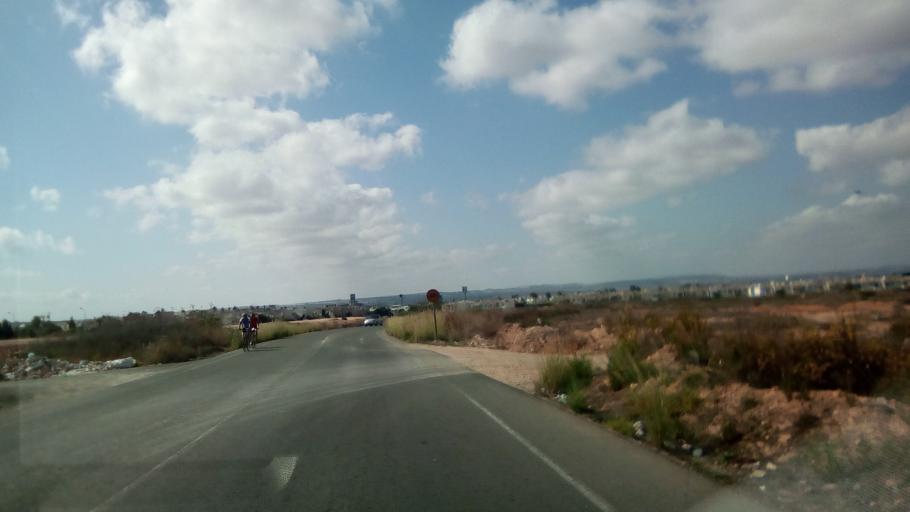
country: ES
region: Valencia
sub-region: Provincia de Alicante
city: Torrevieja
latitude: 38.0002
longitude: -0.6806
